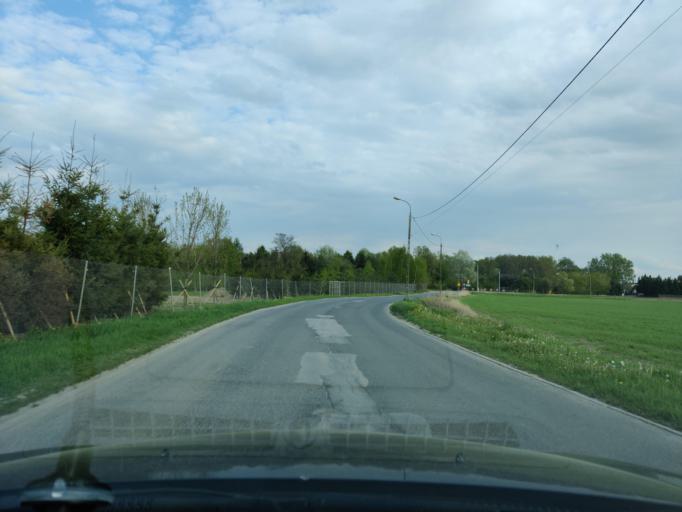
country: PL
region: Masovian Voivodeship
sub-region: Powiat piaseczynski
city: Konstancin-Jeziorna
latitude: 52.1309
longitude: 21.1367
